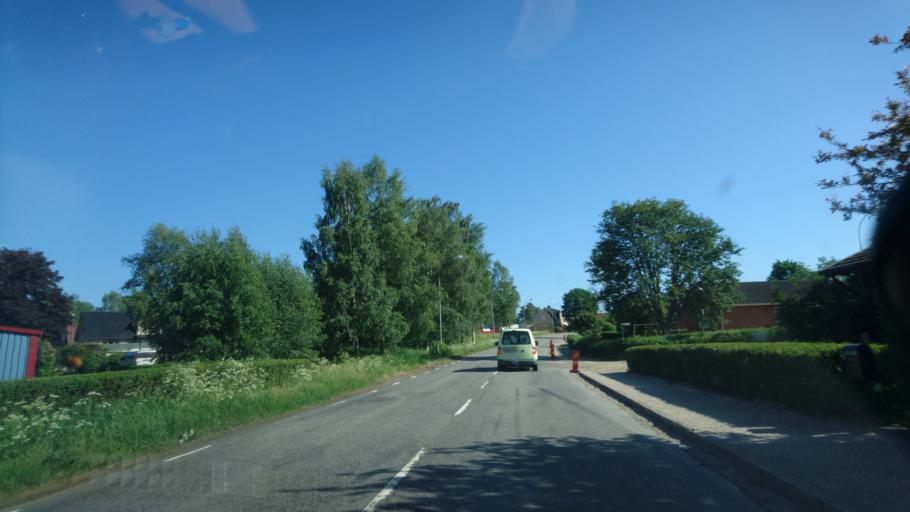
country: SE
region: Skane
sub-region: Osby Kommun
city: Lonsboda
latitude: 56.4036
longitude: 14.3189
